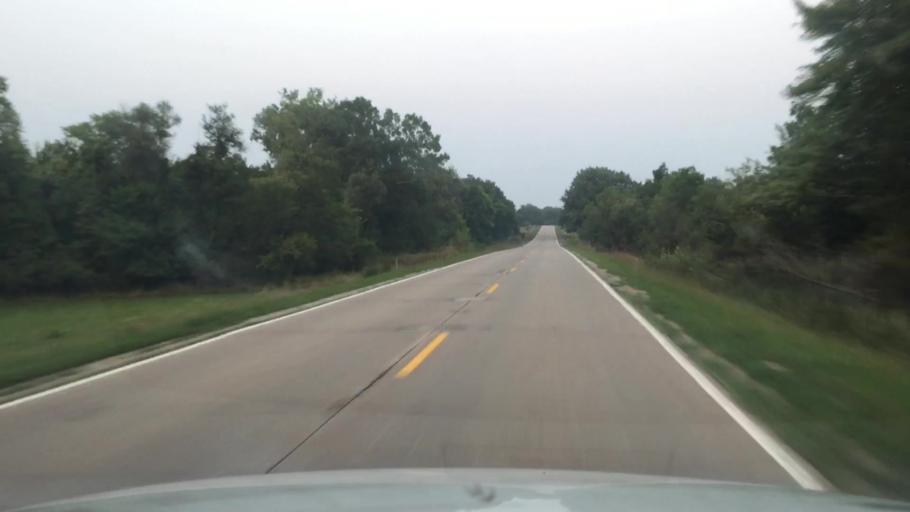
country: US
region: Iowa
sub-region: Warren County
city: Indianola
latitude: 41.1909
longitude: -93.6440
